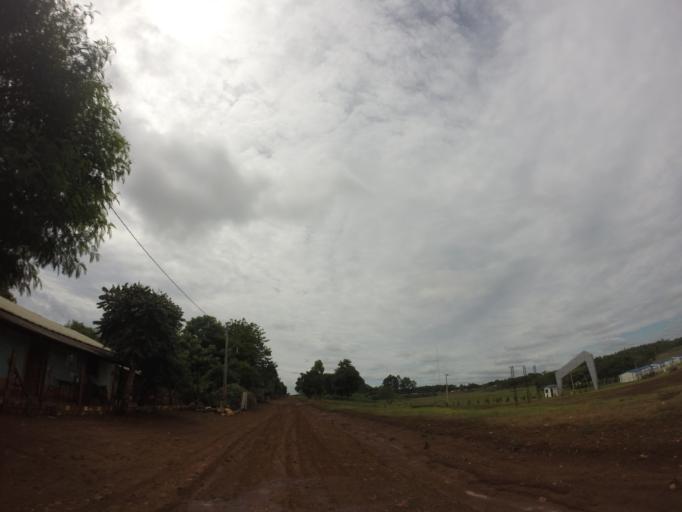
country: PY
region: Alto Parana
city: Ciudad del Este
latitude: -25.3859
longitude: -54.6667
